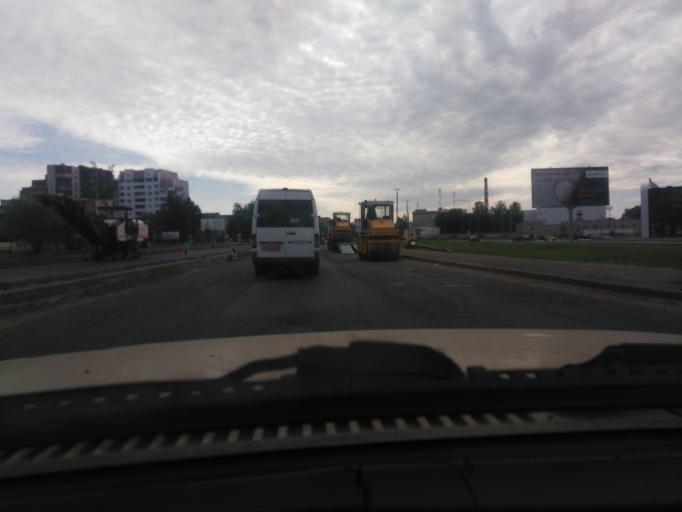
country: BY
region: Mogilev
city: Mahilyow
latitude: 53.9191
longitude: 30.3000
